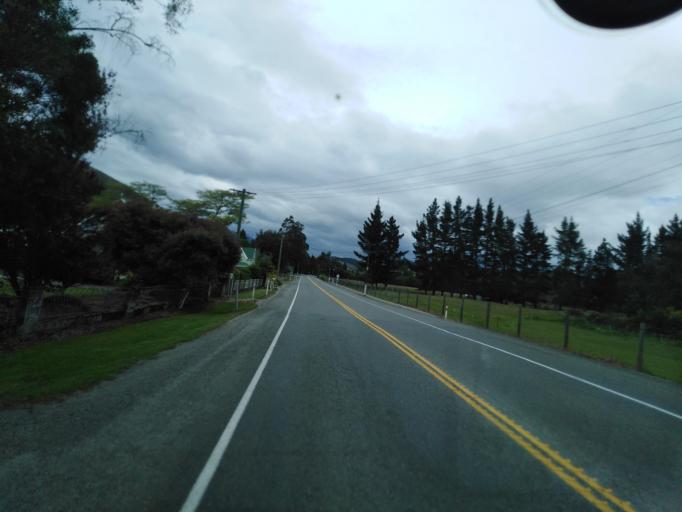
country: NZ
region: Tasman
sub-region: Tasman District
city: Wakefield
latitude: -41.4510
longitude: 172.9579
